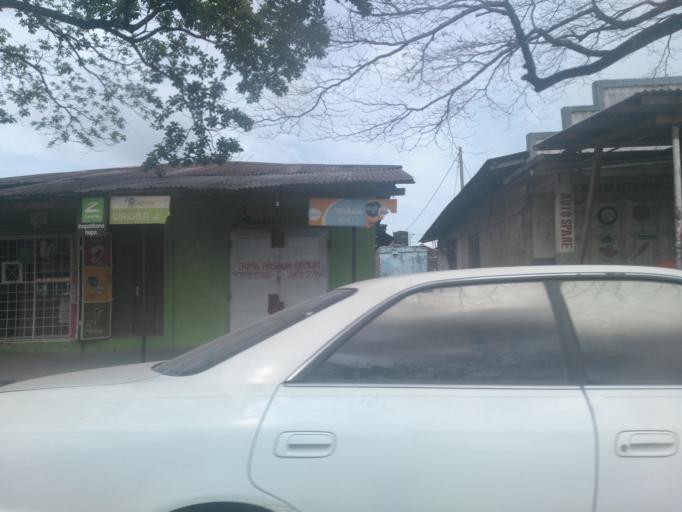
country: TZ
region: Zanzibar Urban/West
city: Zanzibar
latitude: -6.1701
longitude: 39.2025
